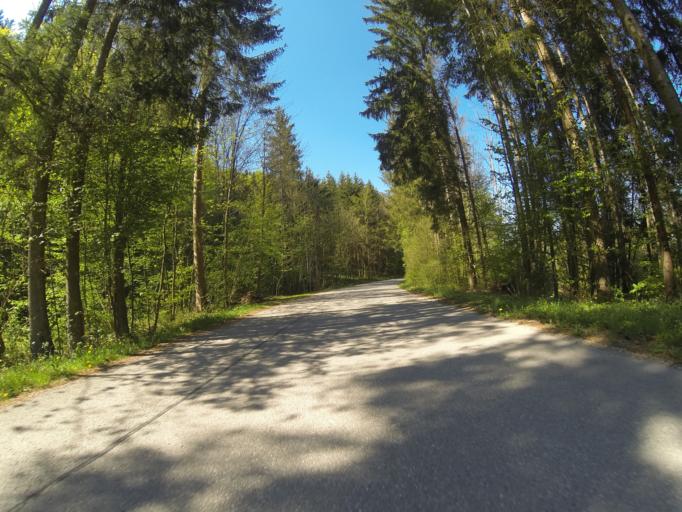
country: AT
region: Upper Austria
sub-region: Politischer Bezirk Gmunden
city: Altmunster
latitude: 47.9424
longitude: 13.7501
